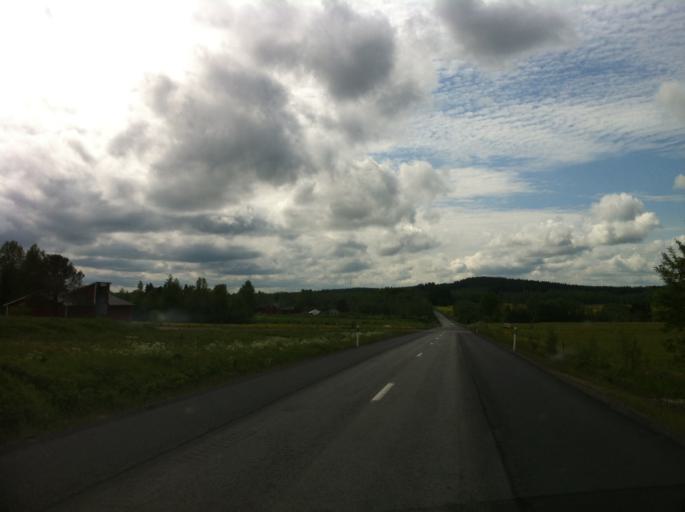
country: SE
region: Vaermland
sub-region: Sunne Kommun
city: Sunne
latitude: 59.7311
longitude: 13.1326
